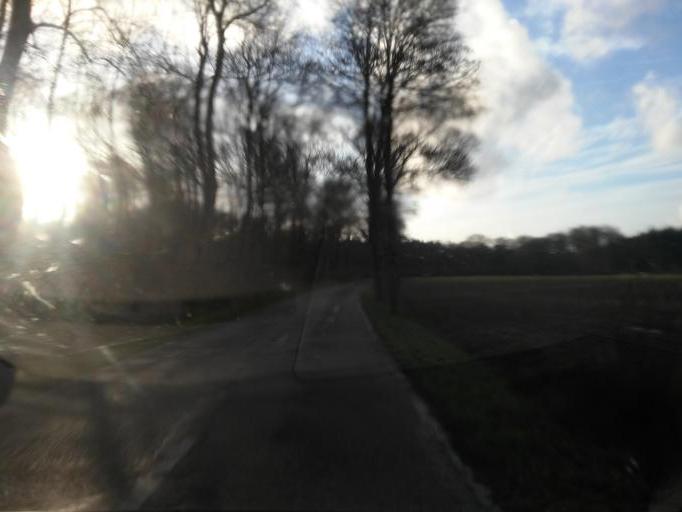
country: BE
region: Wallonia
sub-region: Province du Luxembourg
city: Tintigny
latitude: 49.6587
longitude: 5.4718
